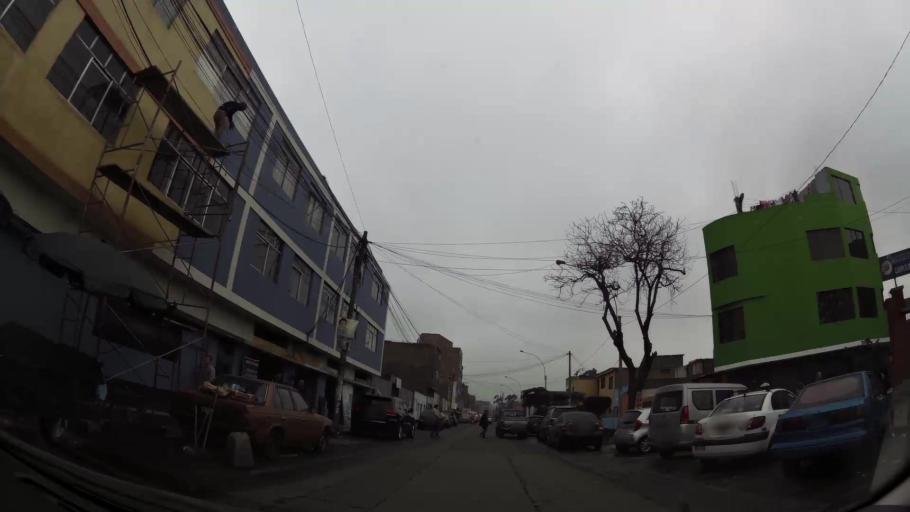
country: PE
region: Lima
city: Lima
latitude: -12.0626
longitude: -77.0263
